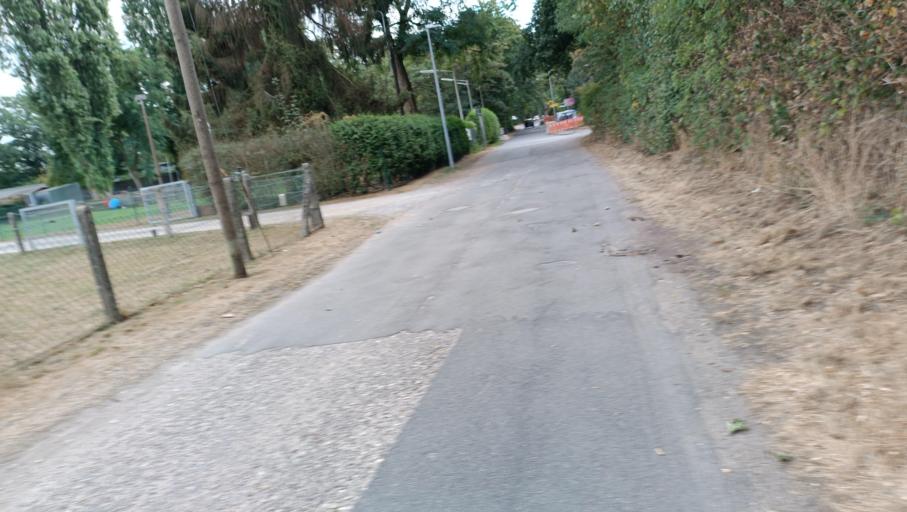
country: DE
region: North Rhine-Westphalia
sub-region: Regierungsbezirk Dusseldorf
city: Moers
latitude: 51.4325
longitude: 6.6504
